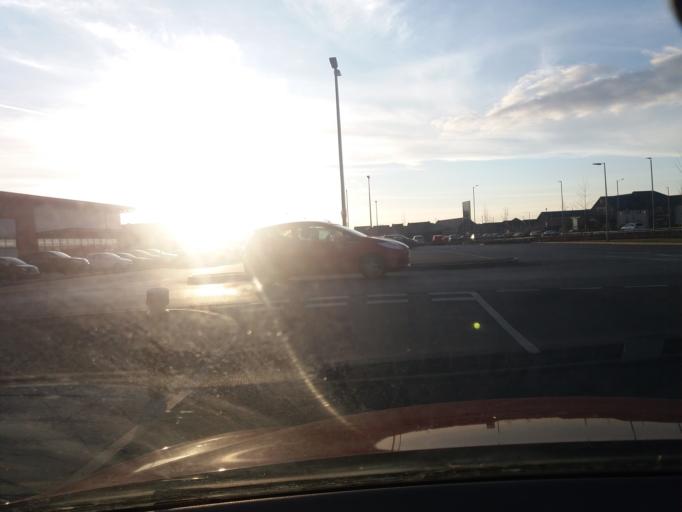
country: GB
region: England
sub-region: Lancashire
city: Euxton
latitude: 53.6761
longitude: -2.6546
